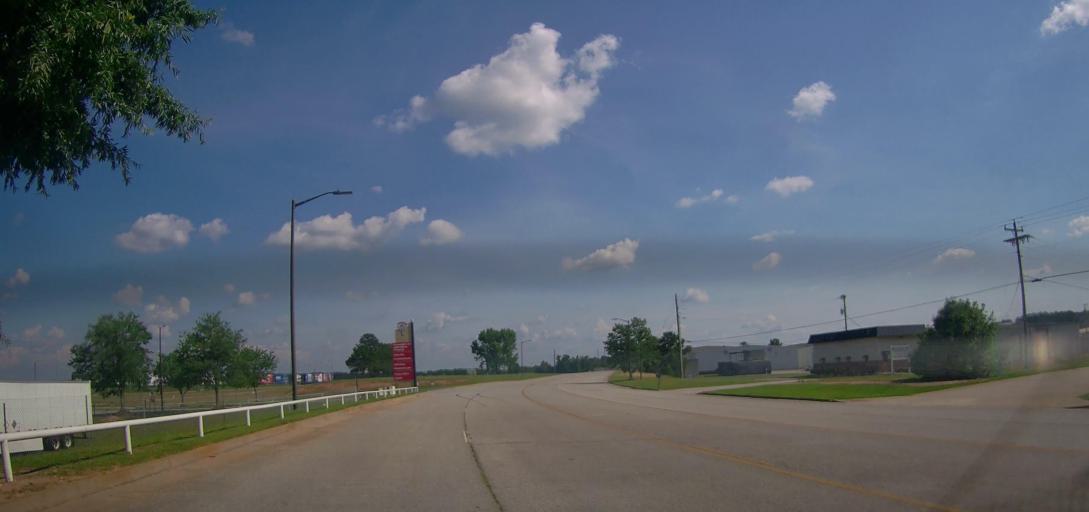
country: US
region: Georgia
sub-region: Henry County
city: Hampton
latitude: 33.3889
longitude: -84.3246
